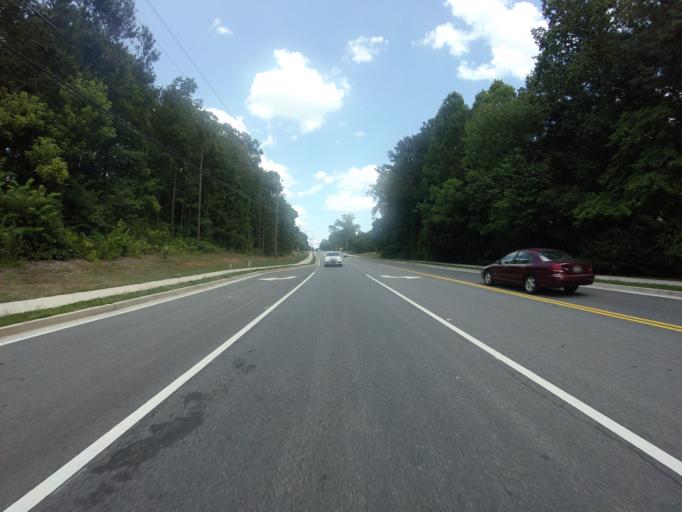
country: US
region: Georgia
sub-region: Fulton County
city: Johns Creek
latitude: 34.0405
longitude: -84.2294
